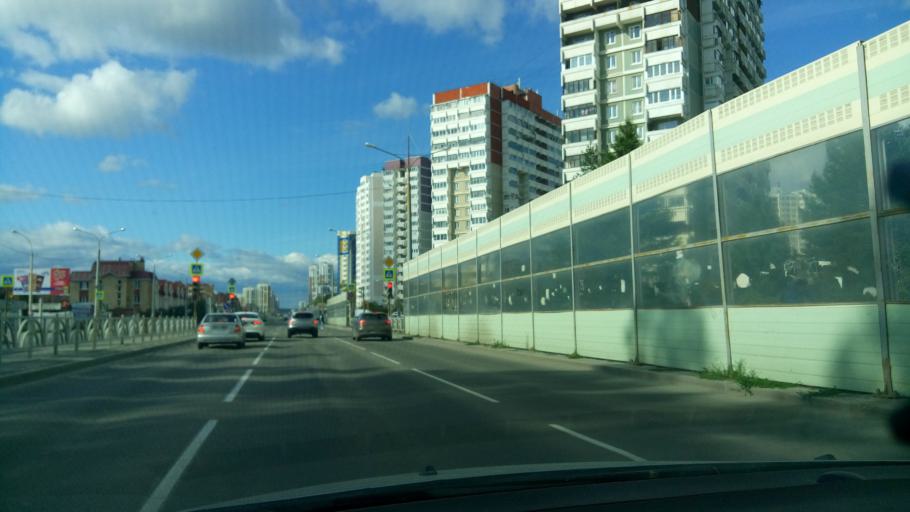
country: RU
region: Sverdlovsk
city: Sovkhoznyy
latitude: 56.7806
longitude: 60.5442
